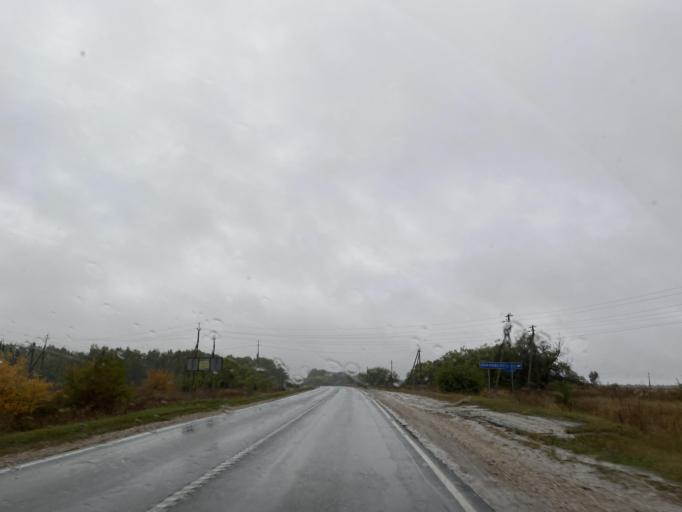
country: RU
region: Rjazan
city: Starozhilovo
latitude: 54.3836
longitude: 39.9255
